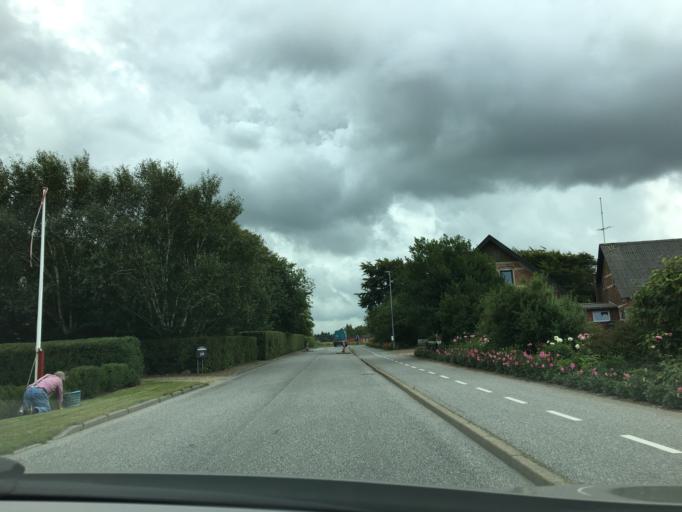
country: DK
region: South Denmark
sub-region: Varde Kommune
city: Oksbol
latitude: 55.7346
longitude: 8.2674
